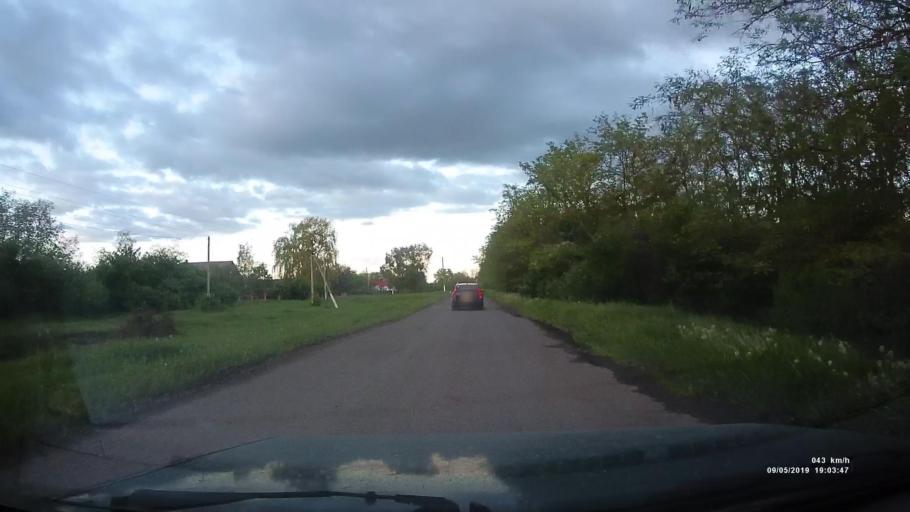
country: RU
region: Krasnodarskiy
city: Kanelovskaya
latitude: 46.7419
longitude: 39.1664
